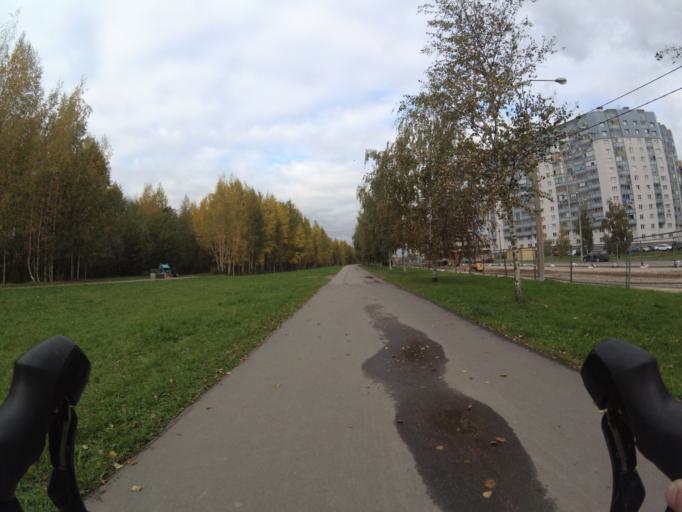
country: RU
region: Leningrad
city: Untolovo
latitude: 59.9980
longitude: 30.1927
